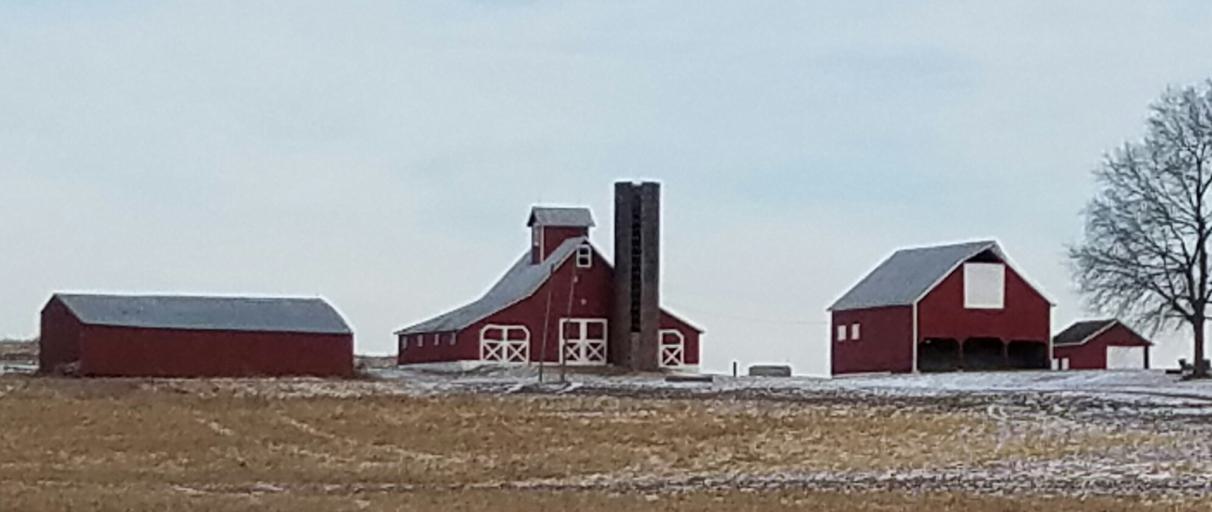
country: US
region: Missouri
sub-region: Lafayette County
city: Lexington
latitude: 39.1841
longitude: -93.7611
